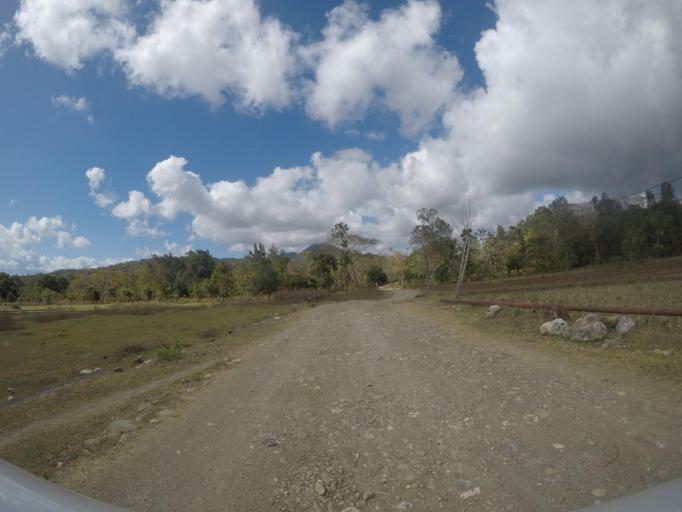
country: TL
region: Lautem
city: Lospalos
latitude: -8.5205
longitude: 126.8409
